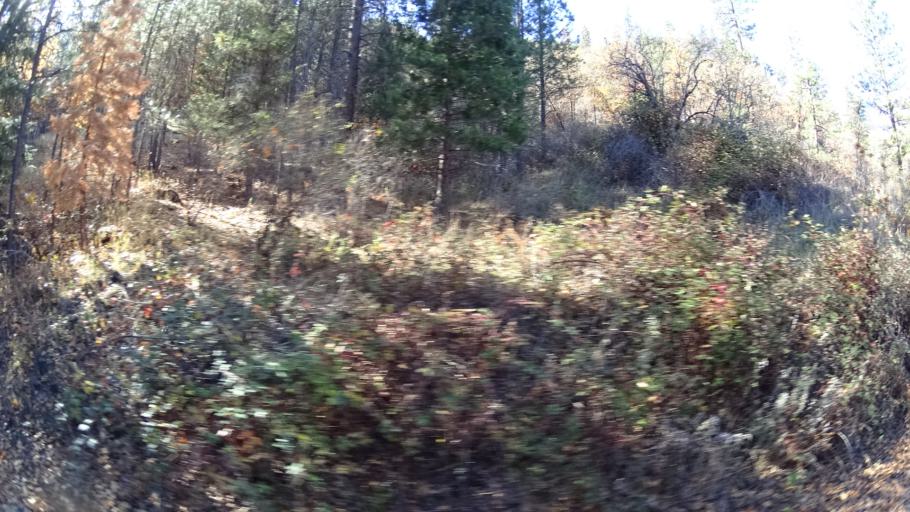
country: US
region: California
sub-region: Siskiyou County
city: Yreka
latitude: 41.8356
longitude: -122.8676
